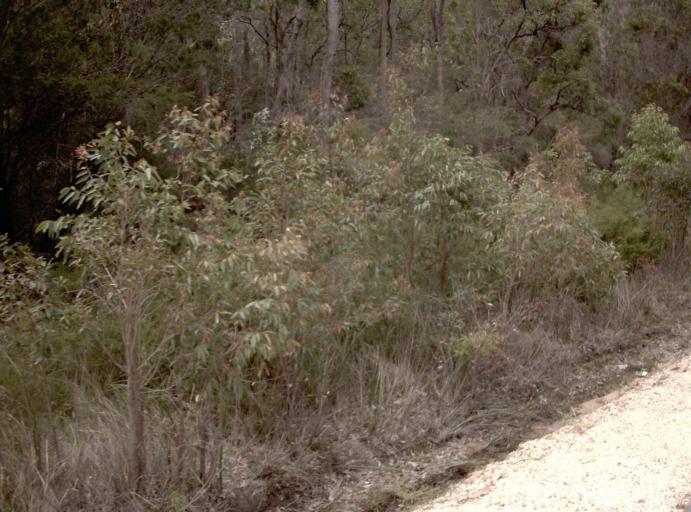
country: AU
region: New South Wales
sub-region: Bega Valley
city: Eden
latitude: -37.4557
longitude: 149.6151
